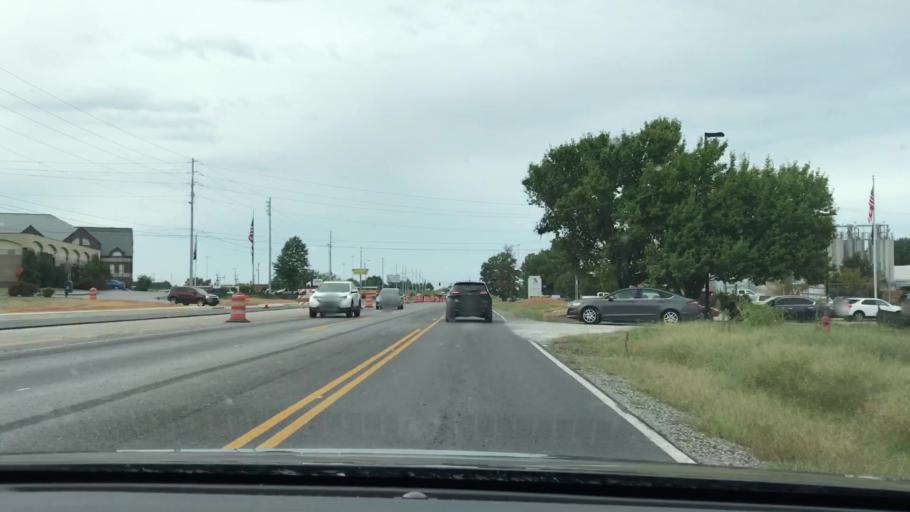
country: US
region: Kentucky
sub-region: Marshall County
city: Benton
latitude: 36.8659
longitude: -88.3565
